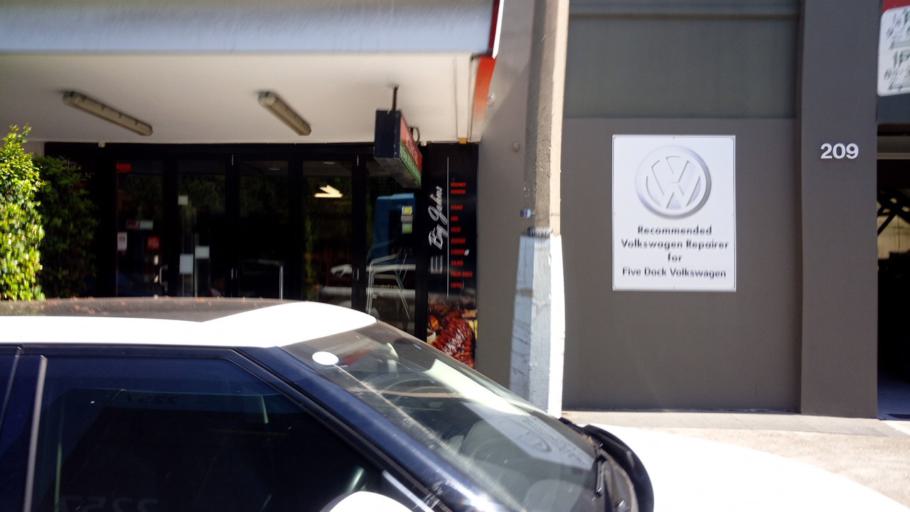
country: AU
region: New South Wales
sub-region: Waverley
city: Bondi
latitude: -33.8943
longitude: 151.2659
